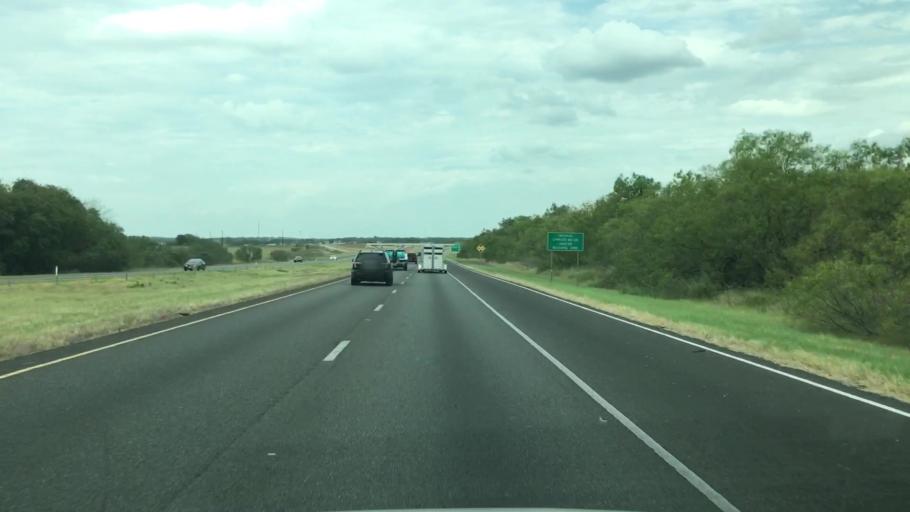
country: US
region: Texas
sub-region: Bexar County
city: Elmendorf
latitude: 29.1341
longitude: -98.4296
